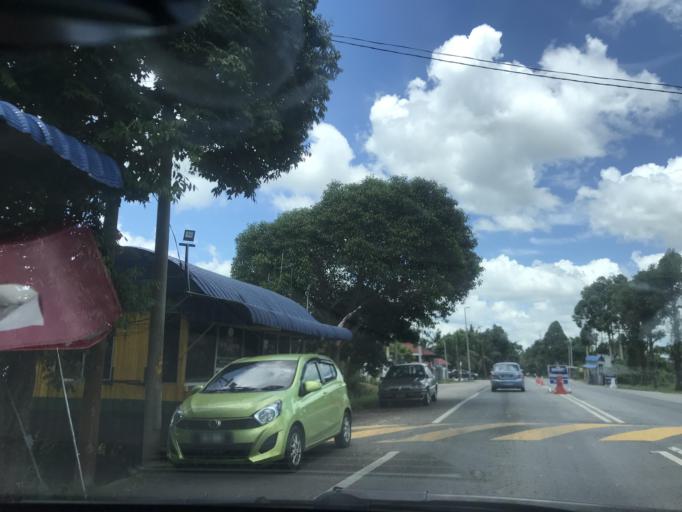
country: MY
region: Kelantan
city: Tumpat
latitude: 6.2096
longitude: 102.1106
